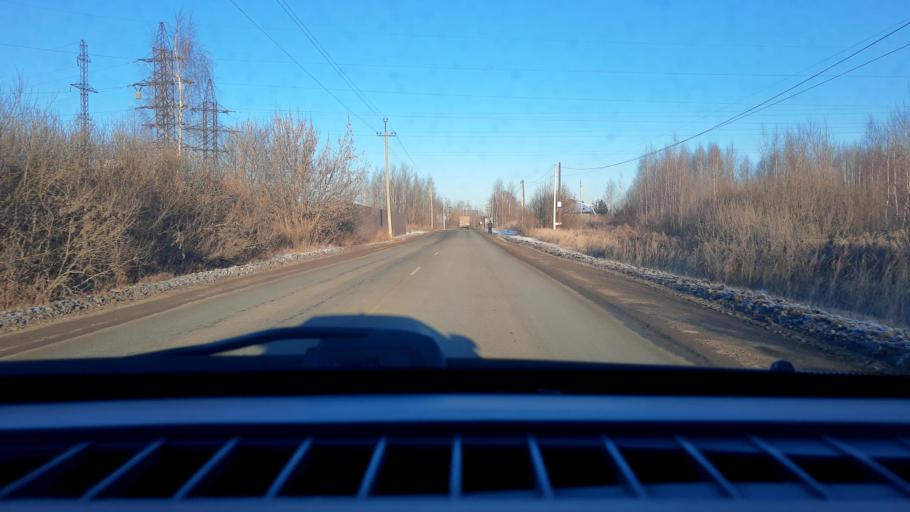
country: RU
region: Nizjnij Novgorod
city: Bor
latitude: 56.3762
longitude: 44.0818
